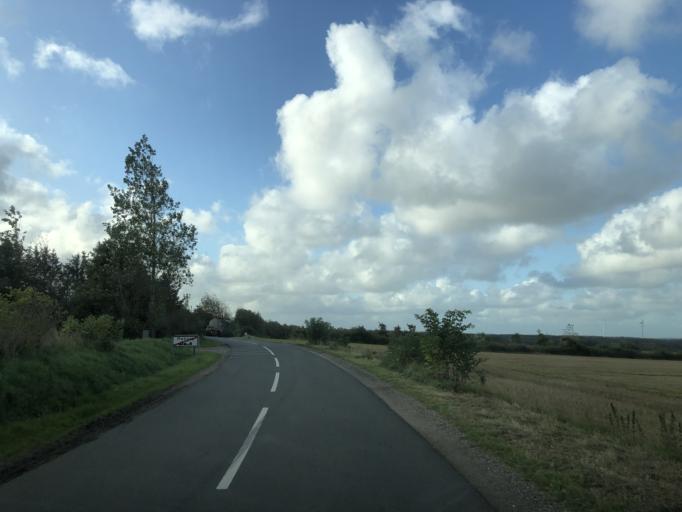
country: DK
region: Central Jutland
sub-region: Holstebro Kommune
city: Ulfborg
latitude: 56.3892
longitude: 8.3497
